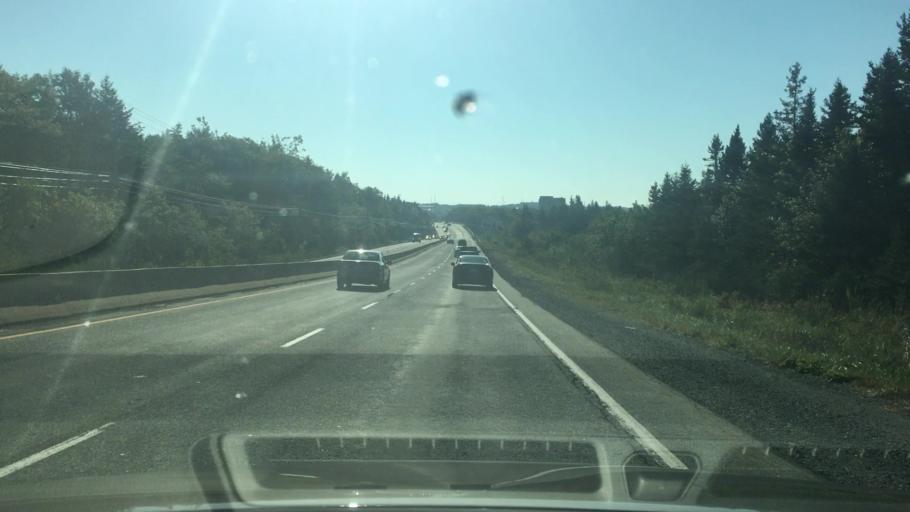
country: CA
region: Nova Scotia
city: Dartmouth
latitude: 44.7081
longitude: -63.6229
